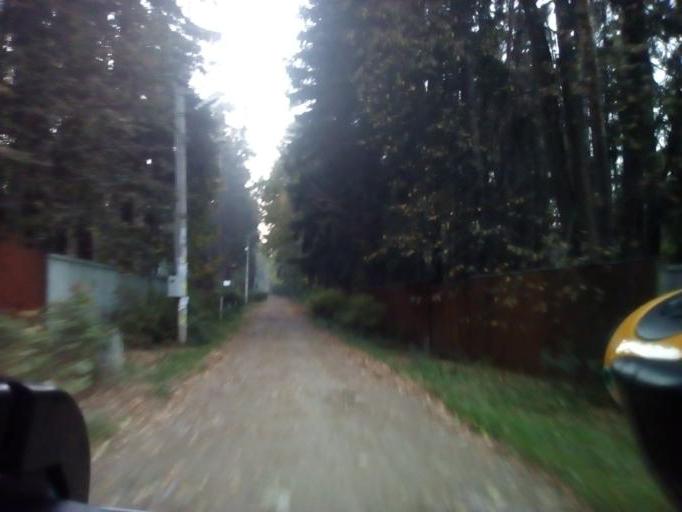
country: RU
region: Moskovskaya
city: Kratovo
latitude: 55.6050
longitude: 38.1732
